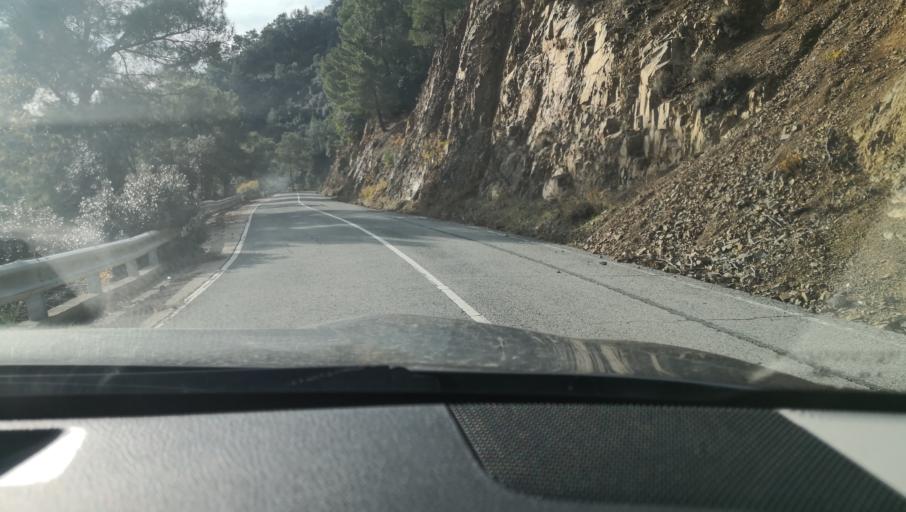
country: CY
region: Lefkosia
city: Lefka
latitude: 35.0143
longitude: 32.7309
